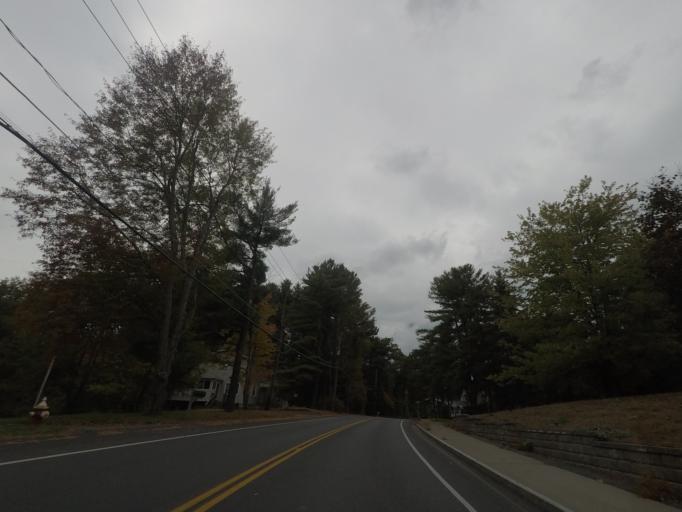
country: US
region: New York
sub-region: Albany County
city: McKownville
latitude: 42.6720
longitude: -73.8473
